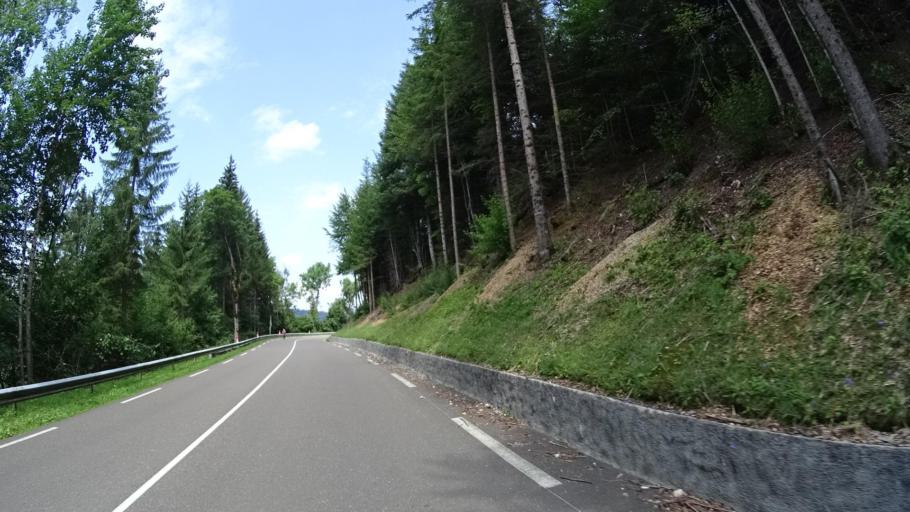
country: FR
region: Franche-Comte
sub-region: Departement du Doubs
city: Les Fourgs
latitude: 46.8129
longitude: 6.3222
